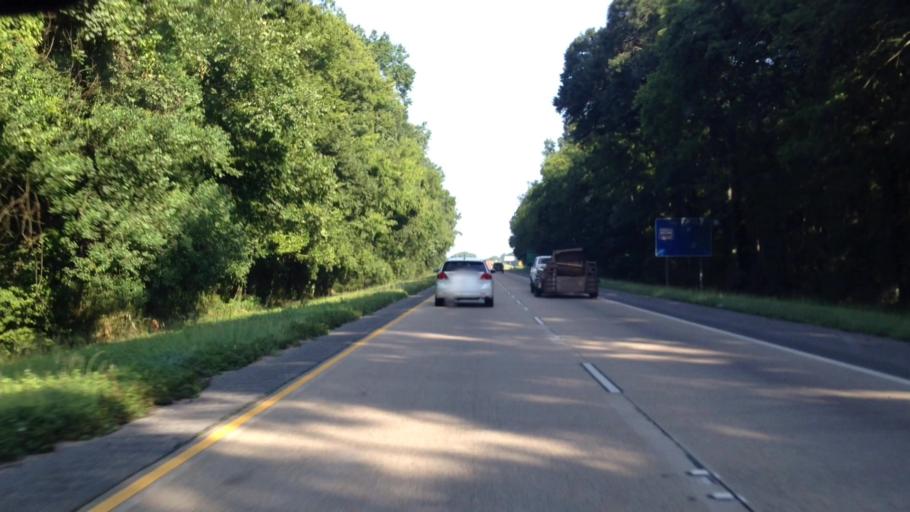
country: US
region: Louisiana
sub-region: Ascension Parish
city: Gonzales
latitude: 30.1886
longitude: -90.9117
